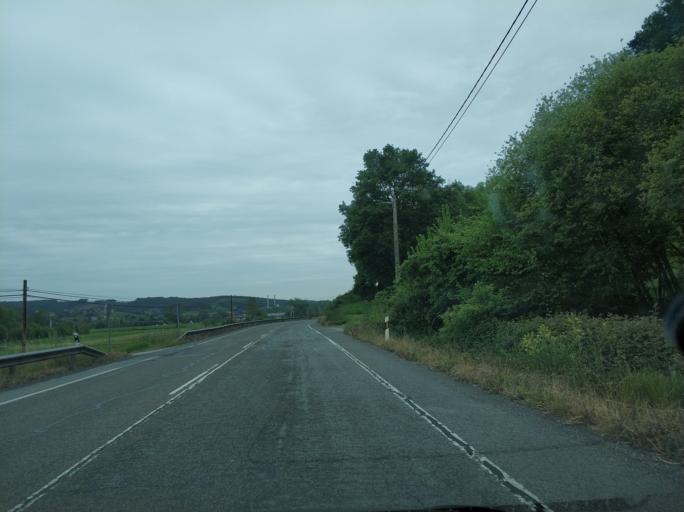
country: ES
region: Cantabria
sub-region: Provincia de Cantabria
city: Puente Viesgo
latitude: 43.3414
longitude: -3.9739
